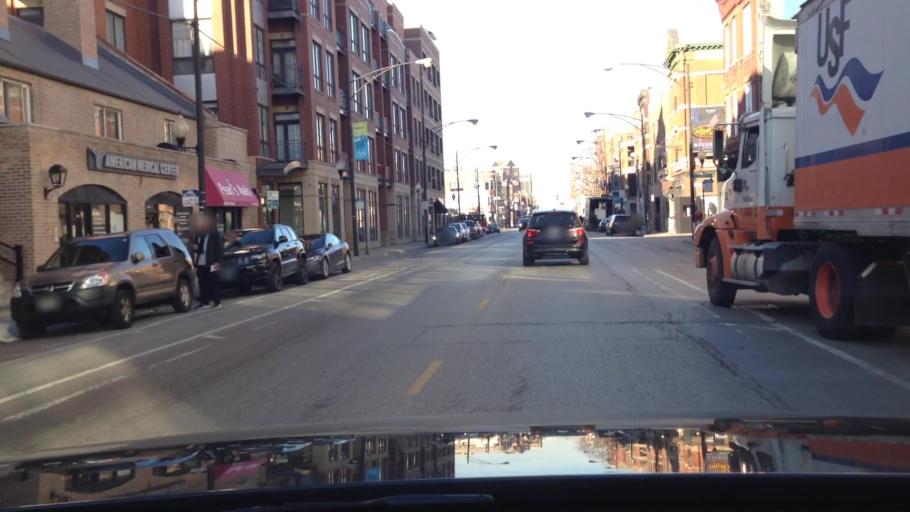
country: US
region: Illinois
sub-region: Cook County
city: Chicago
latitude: 41.9310
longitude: -87.6490
